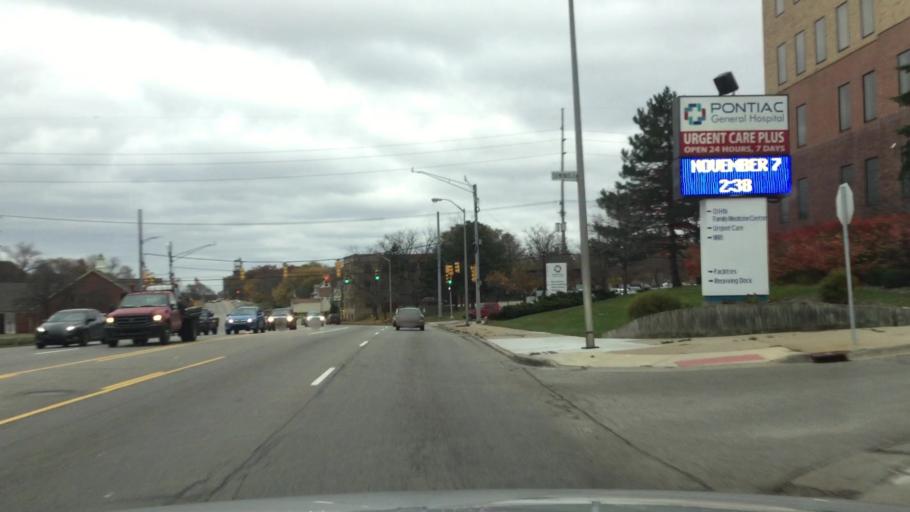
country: US
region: Michigan
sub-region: Oakland County
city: Pontiac
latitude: 42.6356
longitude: -83.3101
